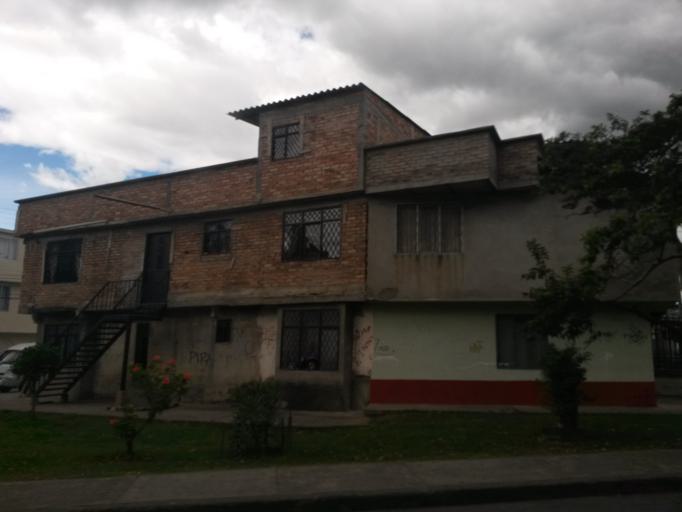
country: CO
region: Cauca
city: Popayan
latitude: 2.4392
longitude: -76.6192
